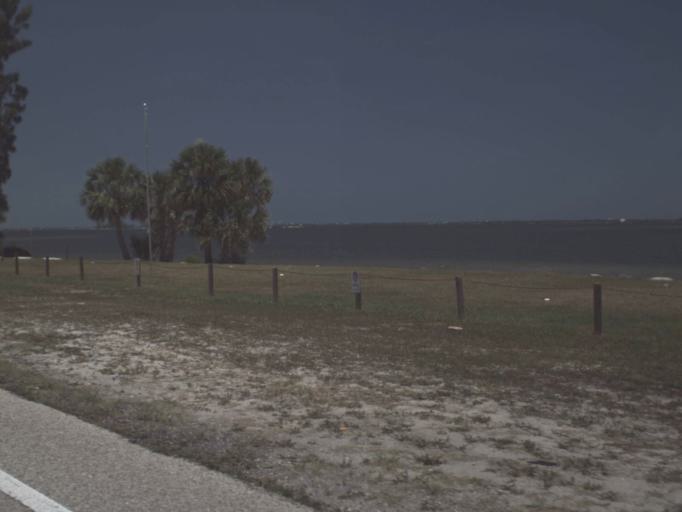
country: US
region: Florida
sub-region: Brevard County
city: Grant-Valkaria
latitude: 27.9635
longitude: -80.5414
